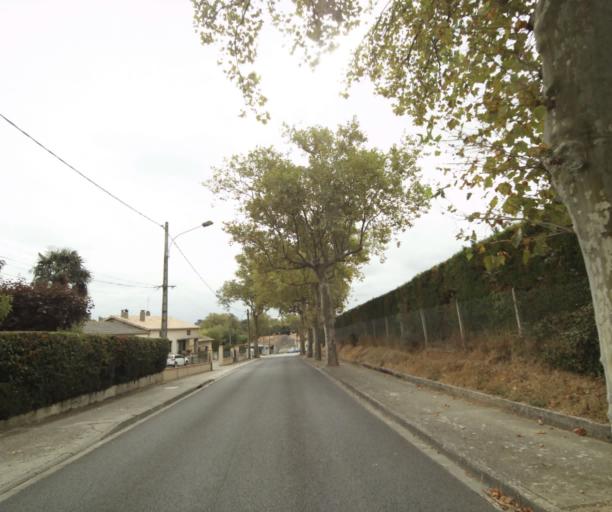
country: FR
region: Midi-Pyrenees
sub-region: Departement de la Haute-Garonne
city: Villefranche-de-Lauragais
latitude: 43.4063
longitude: 1.7172
